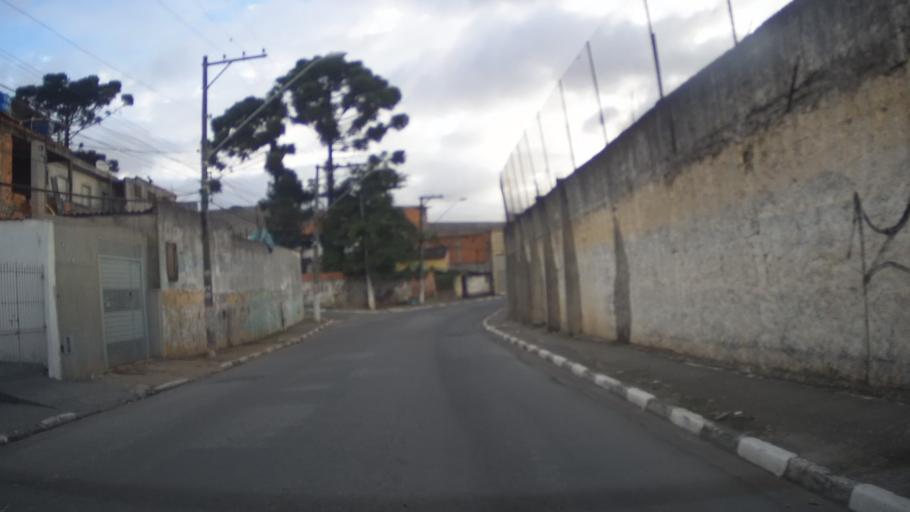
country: BR
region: Sao Paulo
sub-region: Itaquaquecetuba
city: Itaquaquecetuba
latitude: -23.4623
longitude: -46.4129
